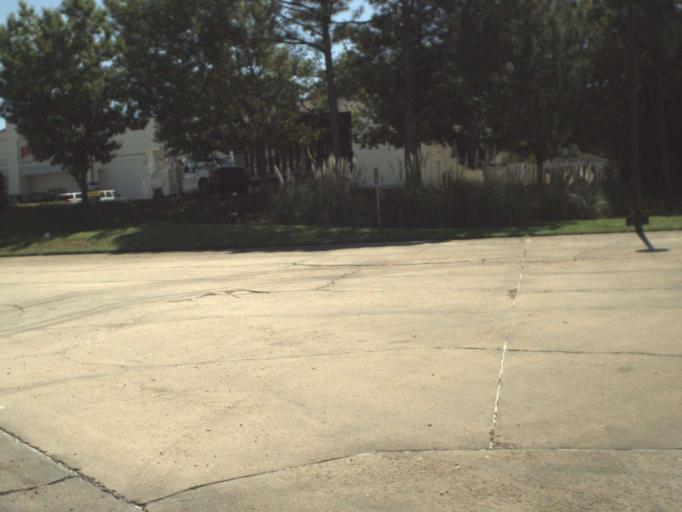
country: US
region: Florida
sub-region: Bay County
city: Panama City
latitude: 30.1580
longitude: -85.6516
